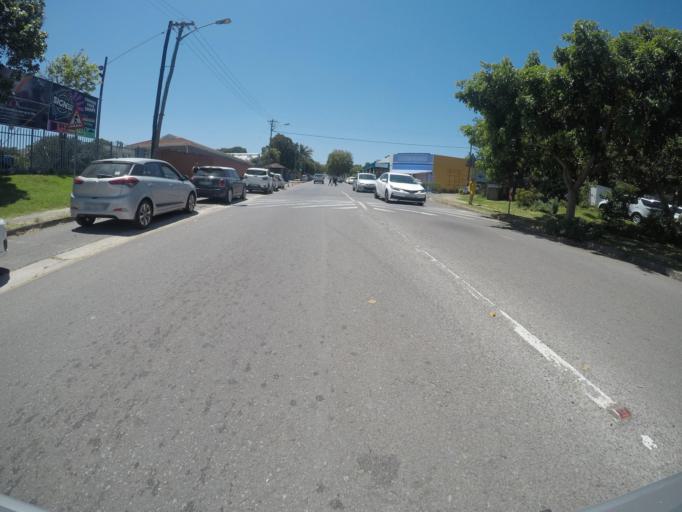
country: ZA
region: Eastern Cape
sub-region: Buffalo City Metropolitan Municipality
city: East London
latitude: -32.9896
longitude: 27.9020
